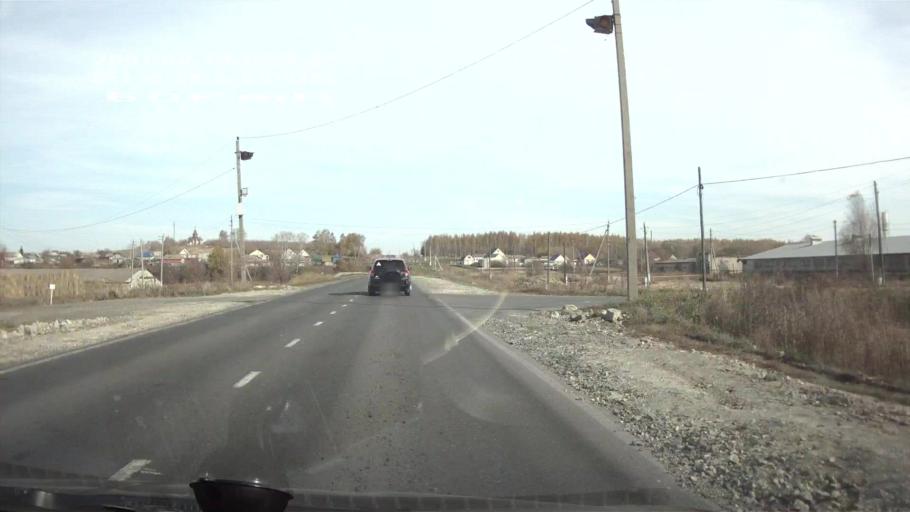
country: RU
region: Mordoviya
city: Atyashevo
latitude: 54.5606
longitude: 45.9768
